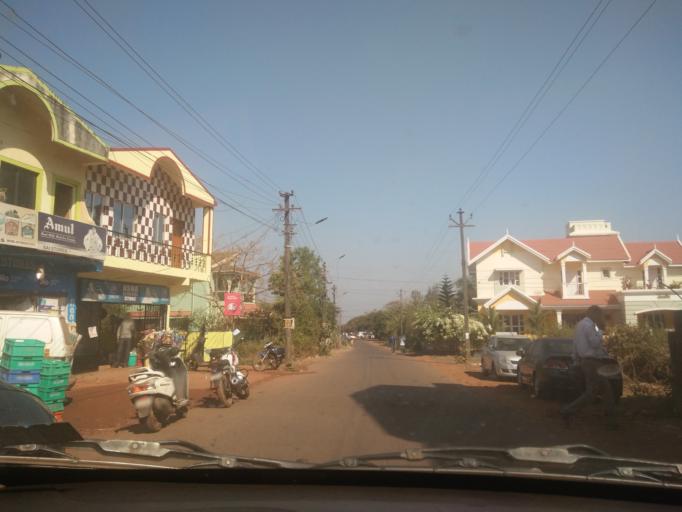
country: IN
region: Goa
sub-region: South Goa
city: Chicalim
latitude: 15.3904
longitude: 73.8640
